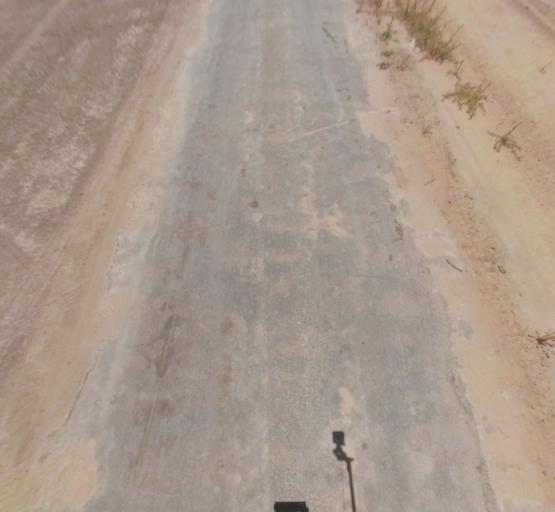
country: US
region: California
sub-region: Madera County
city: Fairmead
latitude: 37.0329
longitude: -120.2098
